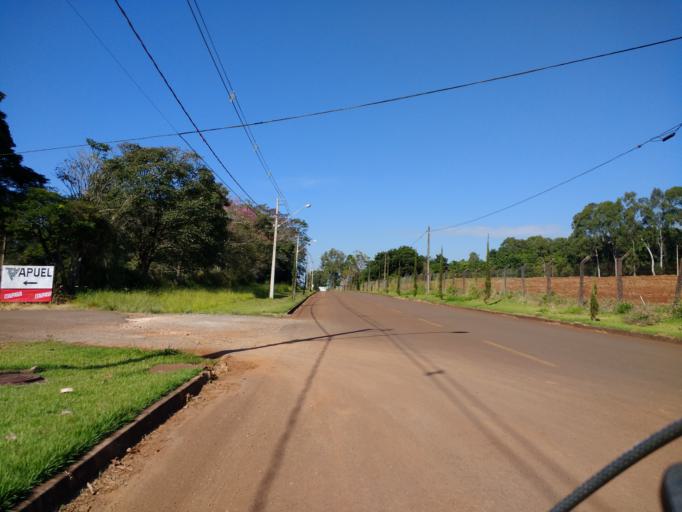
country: BR
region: Parana
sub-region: Londrina
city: Londrina
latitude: -23.3632
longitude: -51.1955
